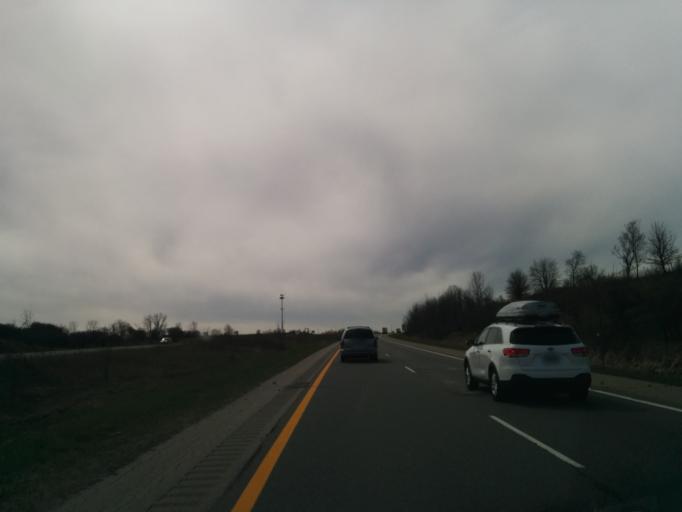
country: US
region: Michigan
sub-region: Ottawa County
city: Zeeland
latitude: 42.7757
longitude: -86.0310
